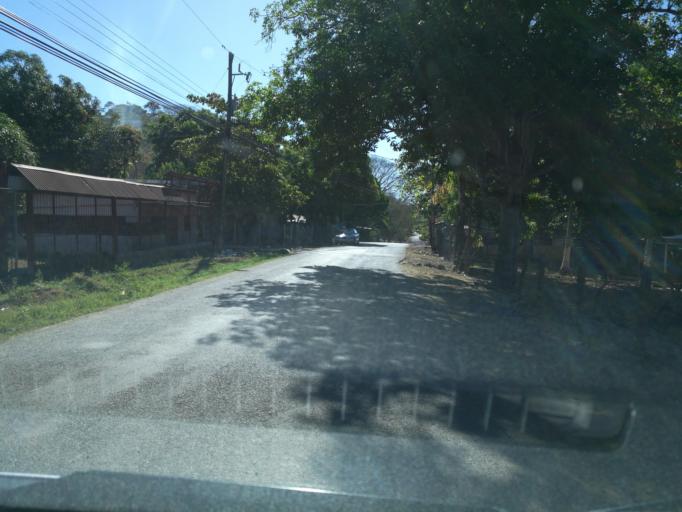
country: CR
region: Guanacaste
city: Juntas
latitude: 10.0978
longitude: -84.9856
